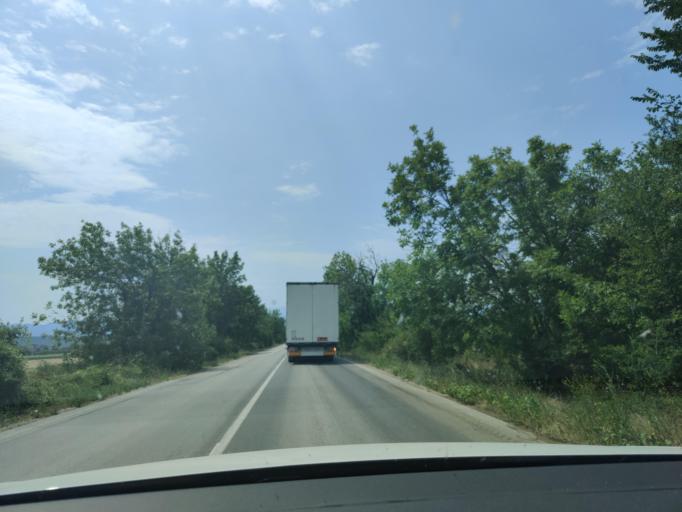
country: BG
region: Vidin
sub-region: Obshtina Ruzhintsi
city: Ruzhintsi
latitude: 43.6281
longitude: 22.8224
